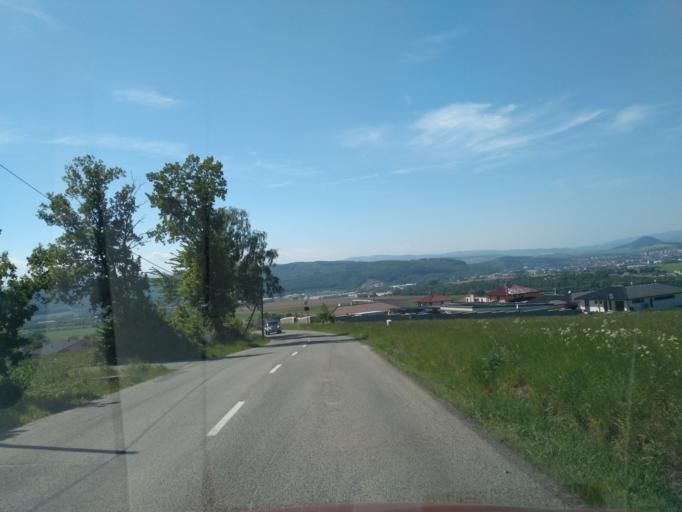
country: SK
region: Presovsky
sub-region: Okres Presov
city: Presov
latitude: 48.9460
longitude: 21.2965
